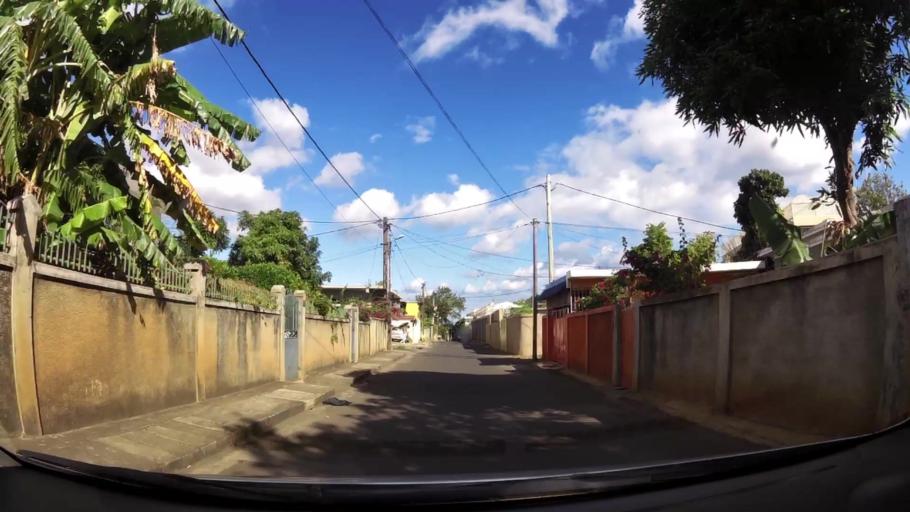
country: MU
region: Pamplemousses
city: Le Hochet
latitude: -20.1493
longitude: 57.5111
